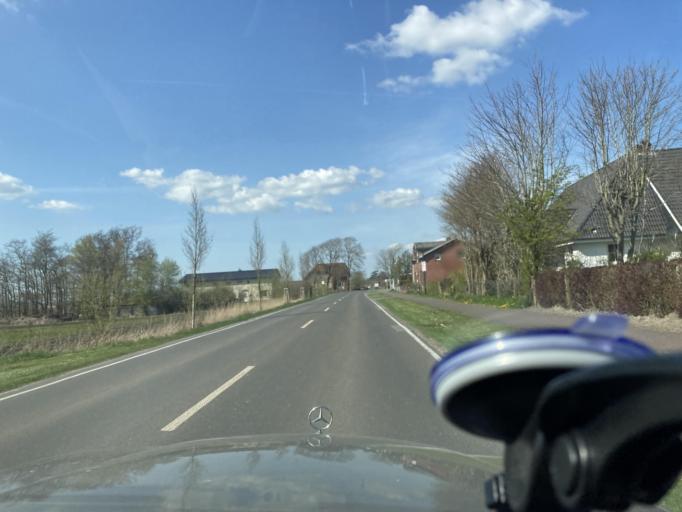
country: DE
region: Schleswig-Holstein
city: Krempel
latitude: 54.3175
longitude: 9.0291
